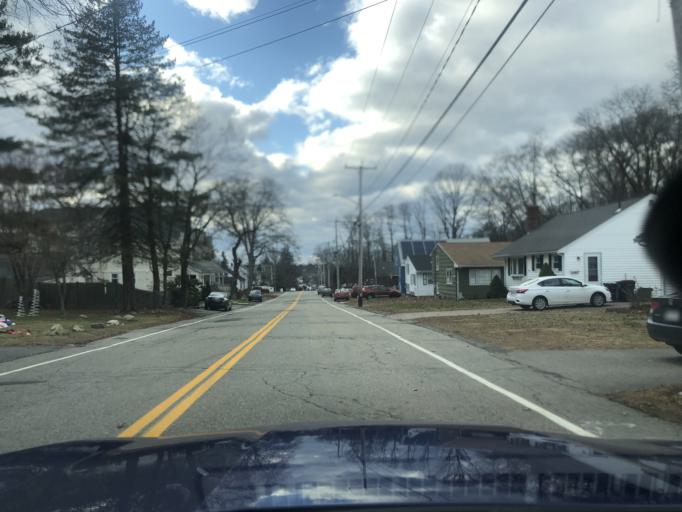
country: US
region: Massachusetts
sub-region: Plymouth County
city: Brockton
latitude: 42.1081
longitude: -71.0103
